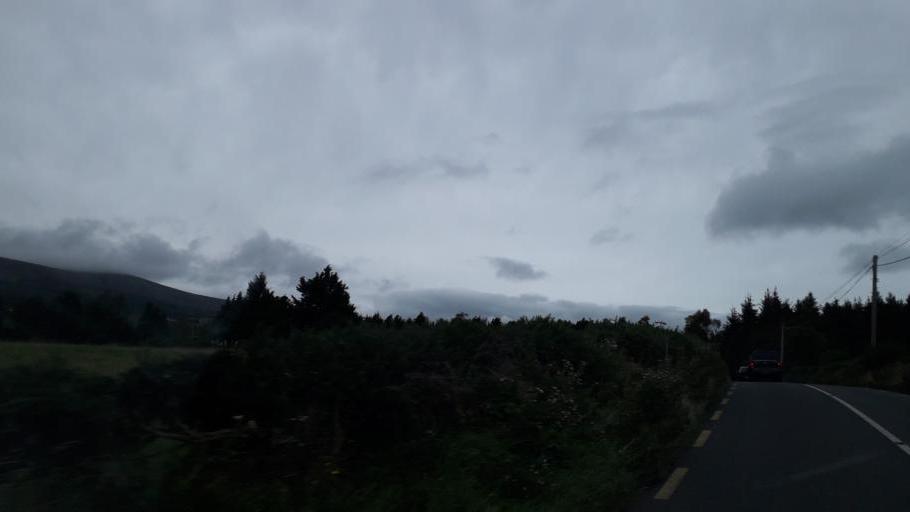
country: IE
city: Newtownmountkennedy
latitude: 53.0921
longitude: -6.2046
